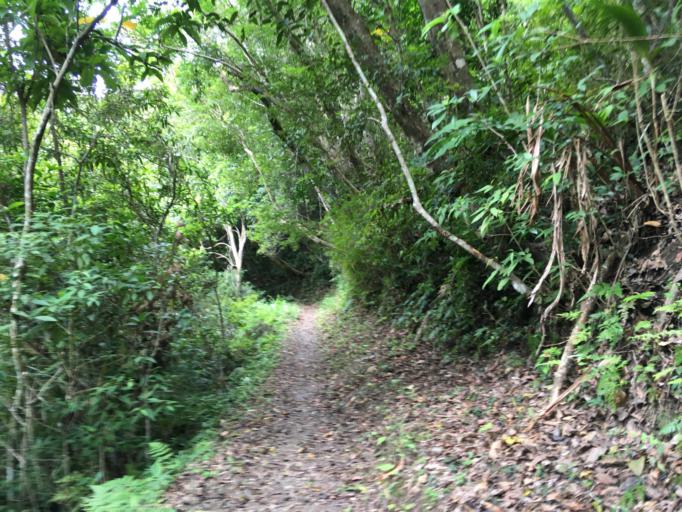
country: TW
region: Taiwan
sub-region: Yilan
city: Yilan
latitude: 24.4262
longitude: 121.7005
